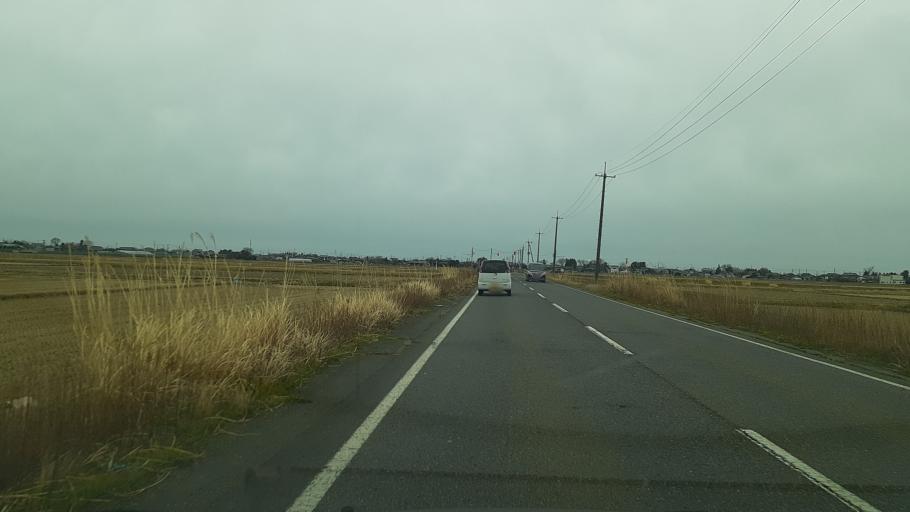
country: JP
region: Niigata
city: Niitsu-honcho
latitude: 37.8284
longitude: 139.0834
